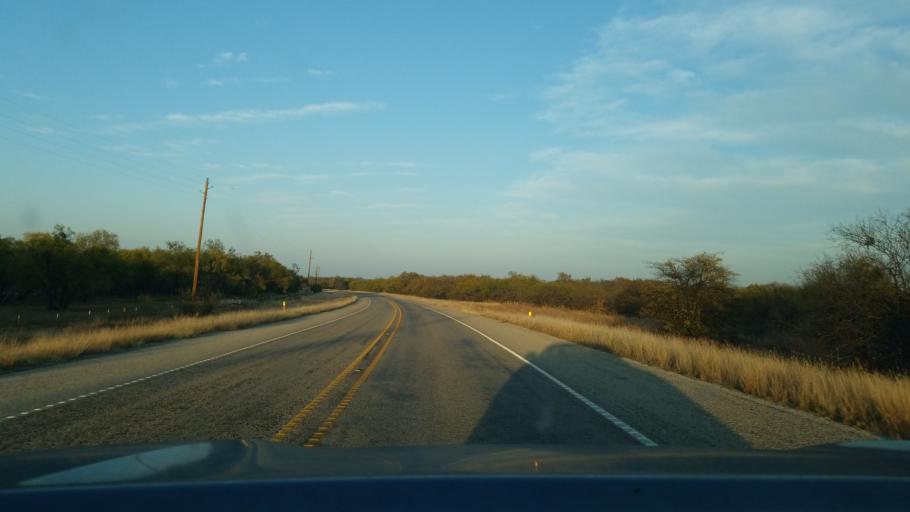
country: US
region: Texas
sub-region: Eastland County
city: Cisco
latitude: 32.4091
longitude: -98.9491
